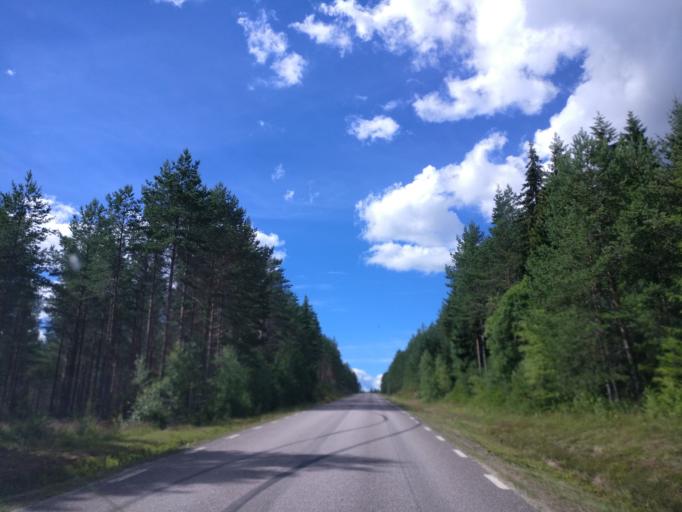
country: SE
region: Vaermland
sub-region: Hagfors Kommun
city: Ekshaerad
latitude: 60.0430
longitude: 13.5201
